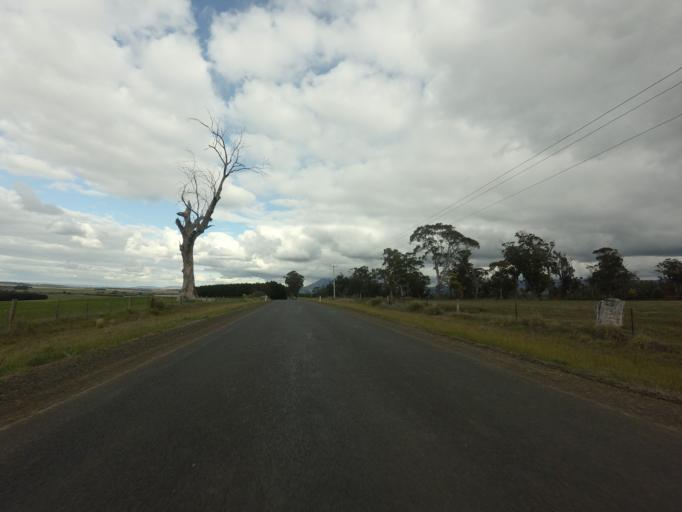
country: AU
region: Tasmania
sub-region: Northern Midlands
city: Longford
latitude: -41.7654
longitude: 147.0844
